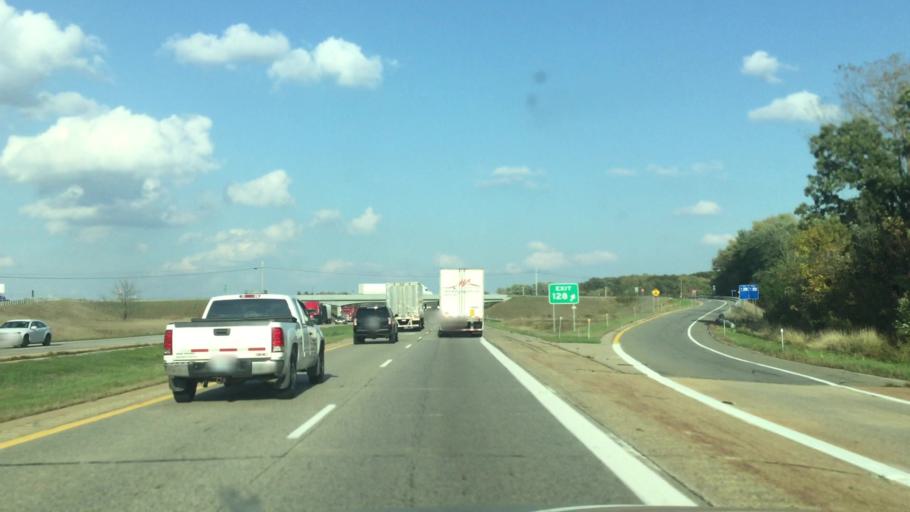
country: US
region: Michigan
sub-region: Jackson County
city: Concord
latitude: 42.2647
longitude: -84.6228
